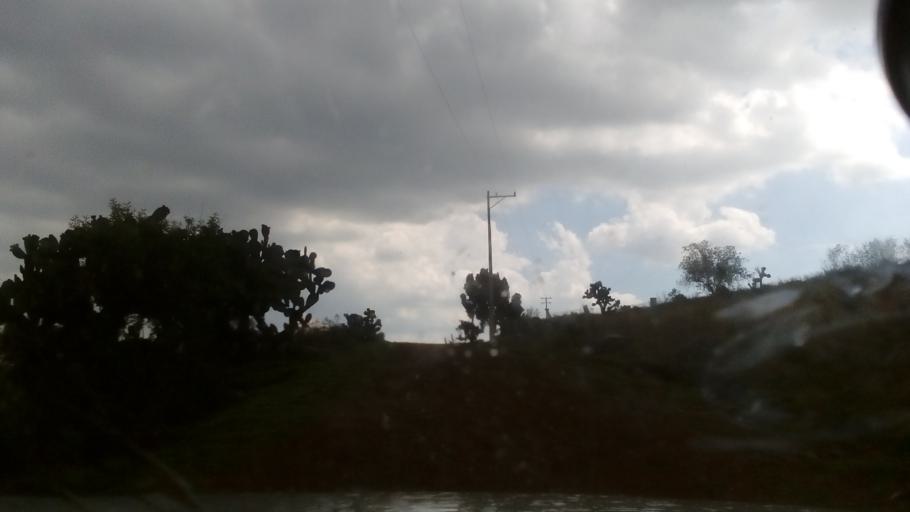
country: MX
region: Guanajuato
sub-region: Silao de la Victoria
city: San Francisco (Banos de Agua Caliente)
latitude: 21.1489
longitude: -101.4361
